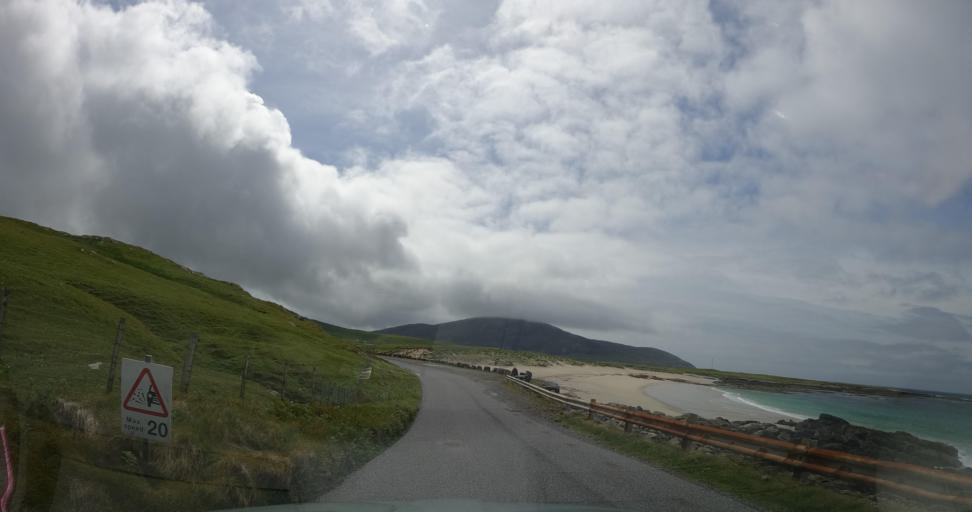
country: GB
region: Scotland
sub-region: Eilean Siar
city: Barra
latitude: 56.9903
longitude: -7.5095
